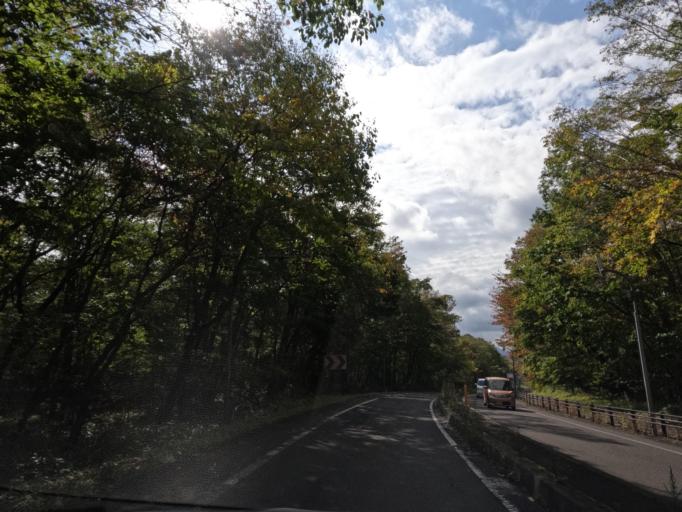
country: JP
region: Hokkaido
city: Chitose
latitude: 42.7970
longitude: 141.5666
